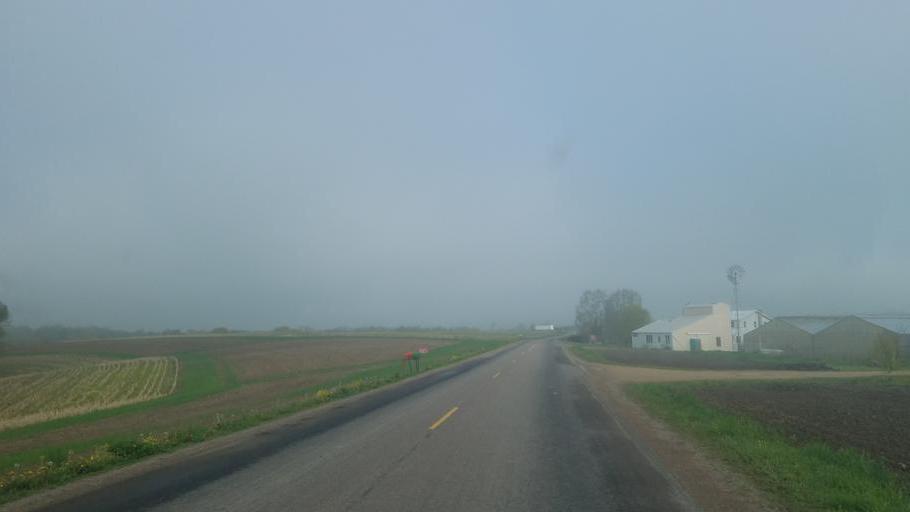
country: US
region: Wisconsin
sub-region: Vernon County
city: Hillsboro
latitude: 43.6134
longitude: -90.4432
